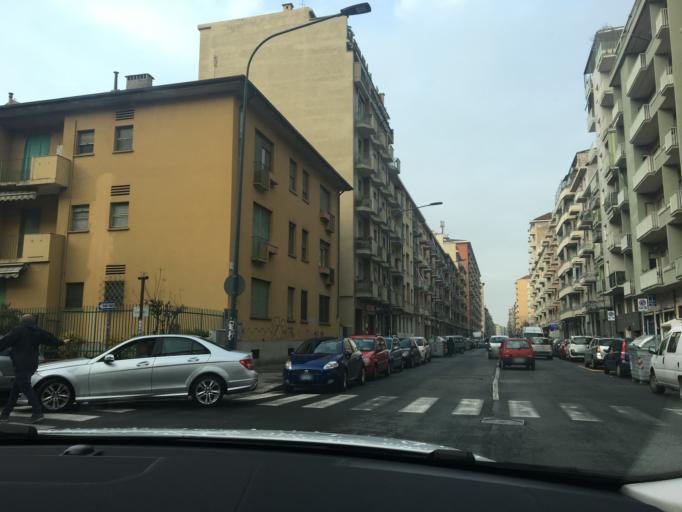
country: IT
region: Piedmont
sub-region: Provincia di Torino
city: Lesna
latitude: 45.0372
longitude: 7.6414
